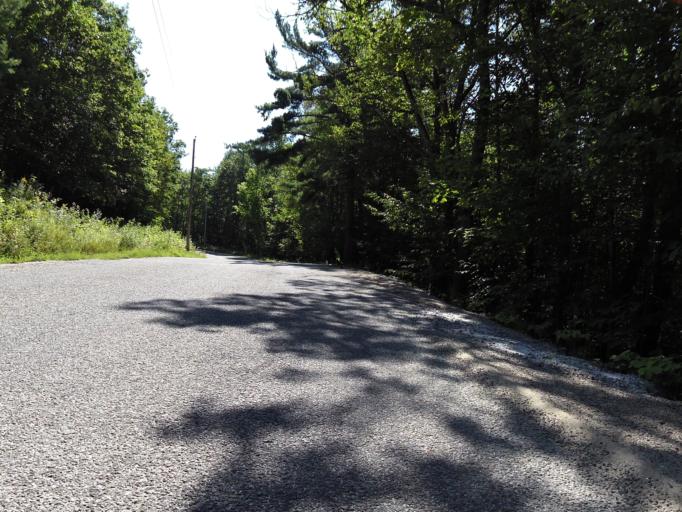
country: CA
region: Quebec
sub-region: Outaouais
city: Maniwaki
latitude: 46.2198
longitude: -76.1047
